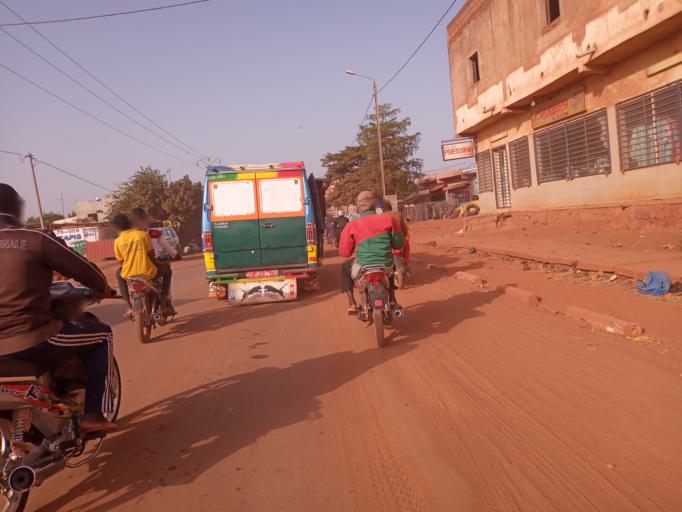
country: ML
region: Bamako
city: Bamako
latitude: 12.5793
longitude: -8.0252
